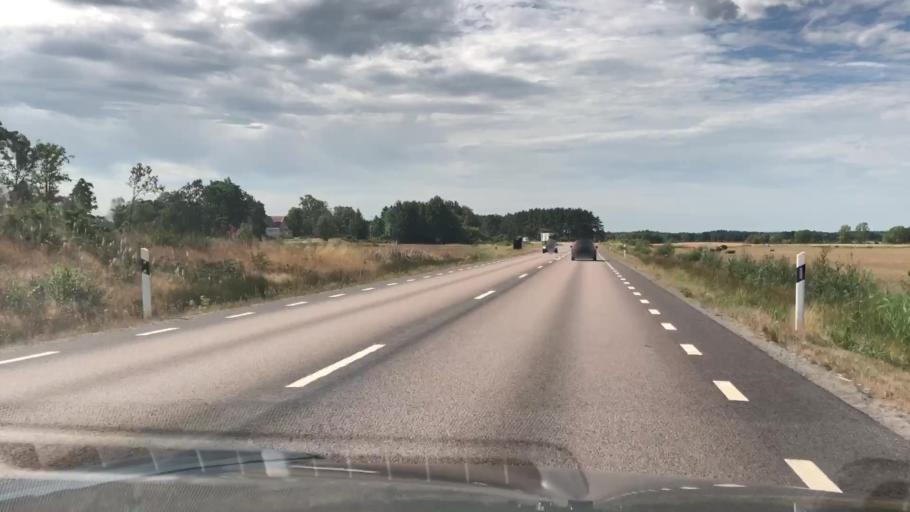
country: SE
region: Kalmar
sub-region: Torsas Kommun
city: Torsas
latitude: 56.3541
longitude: 16.0555
